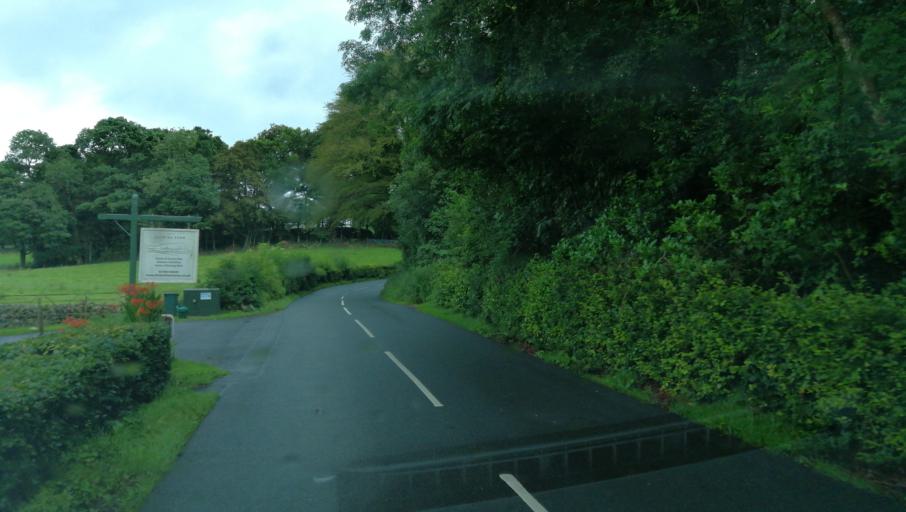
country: GB
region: England
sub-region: Cumbria
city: Penrith
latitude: 54.5876
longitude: -2.8655
